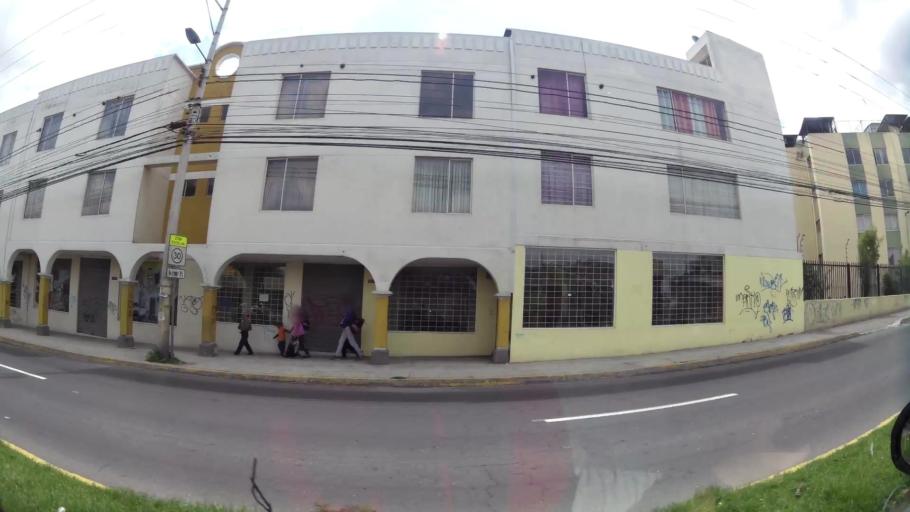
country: EC
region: Pichincha
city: Quito
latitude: -0.1028
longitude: -78.4509
